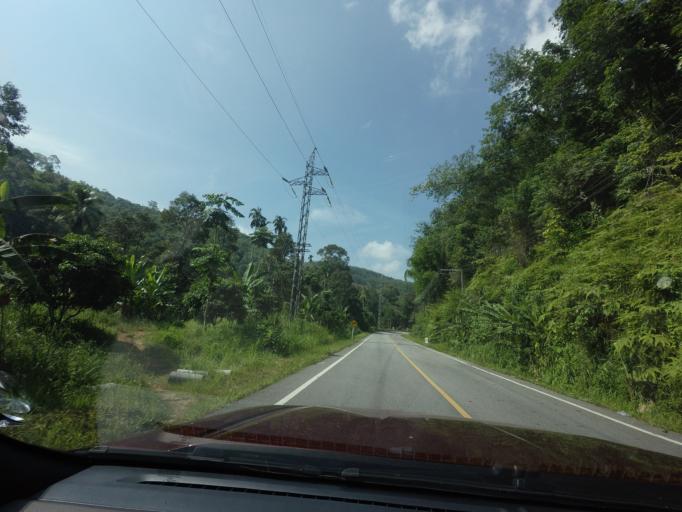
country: TH
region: Yala
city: Betong
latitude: 5.9284
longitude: 101.1869
